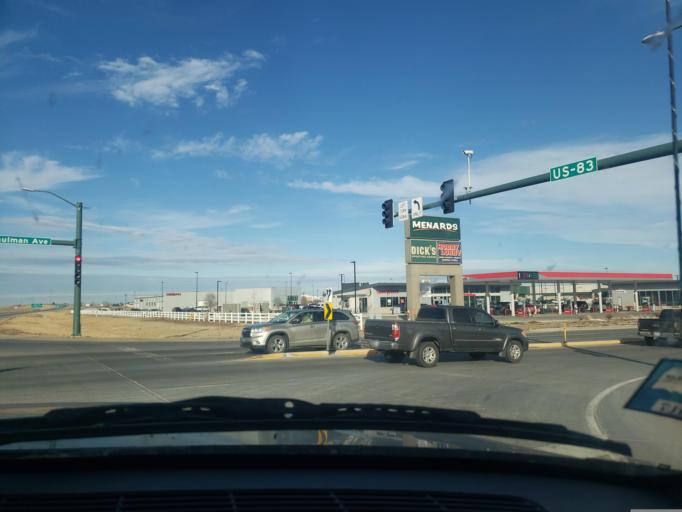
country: US
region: Kansas
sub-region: Finney County
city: Garden City
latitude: 37.9746
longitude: -100.8384
